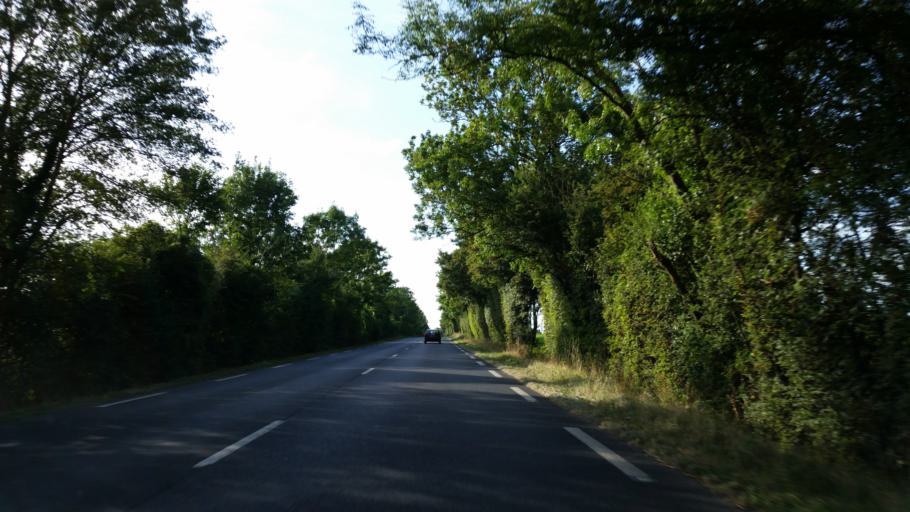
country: FR
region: Lower Normandy
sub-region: Departement du Calvados
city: Cambremer
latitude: 49.1347
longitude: -0.0029
